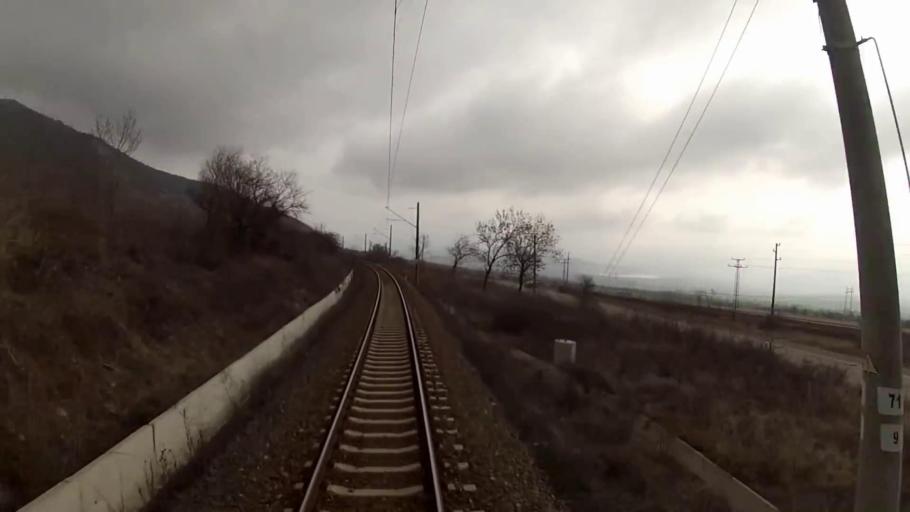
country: BG
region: Sofiya
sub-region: Obshtina Chelopech
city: Chelopech
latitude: 42.6926
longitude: 24.0425
